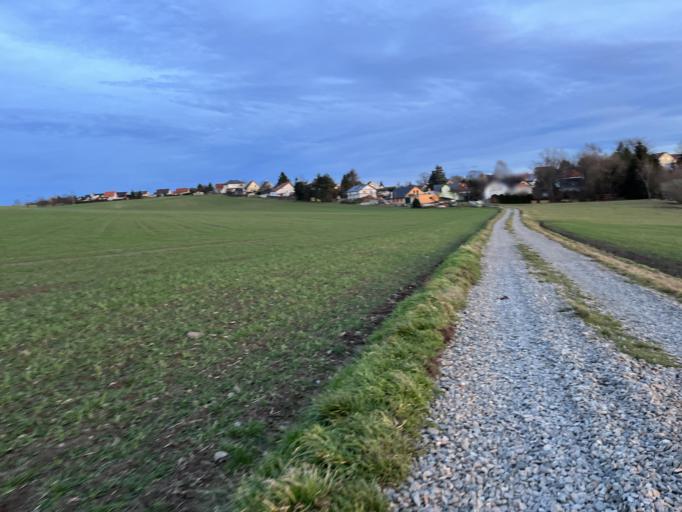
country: DE
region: Saxony
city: Tharandt
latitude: 51.0187
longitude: 13.5653
